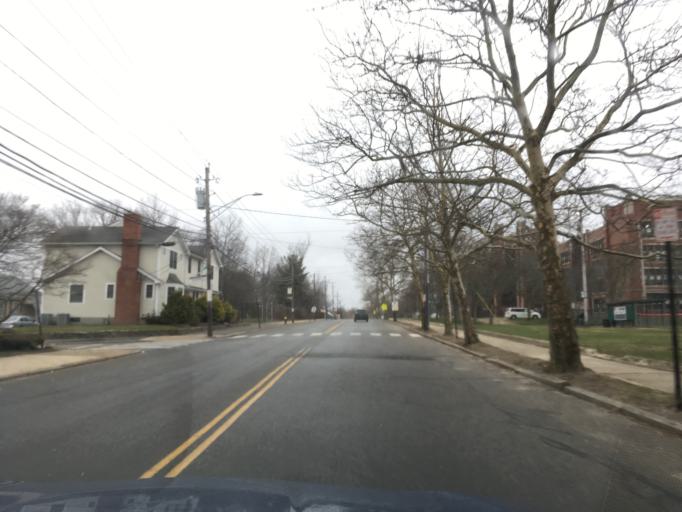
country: US
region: Rhode Island
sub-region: Providence County
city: North Providence
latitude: 41.8413
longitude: -71.4527
